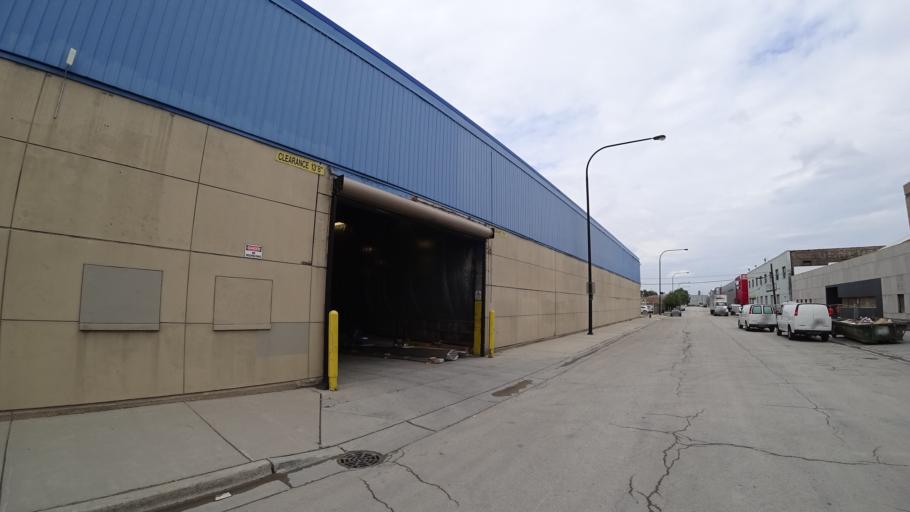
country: US
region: Illinois
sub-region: Cook County
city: Cicero
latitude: 41.8614
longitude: -87.7631
